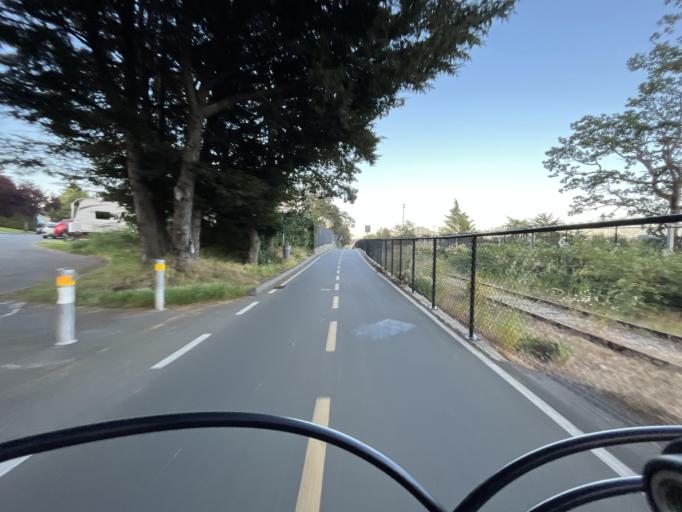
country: CA
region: British Columbia
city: Victoria
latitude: 48.4378
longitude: -123.4252
